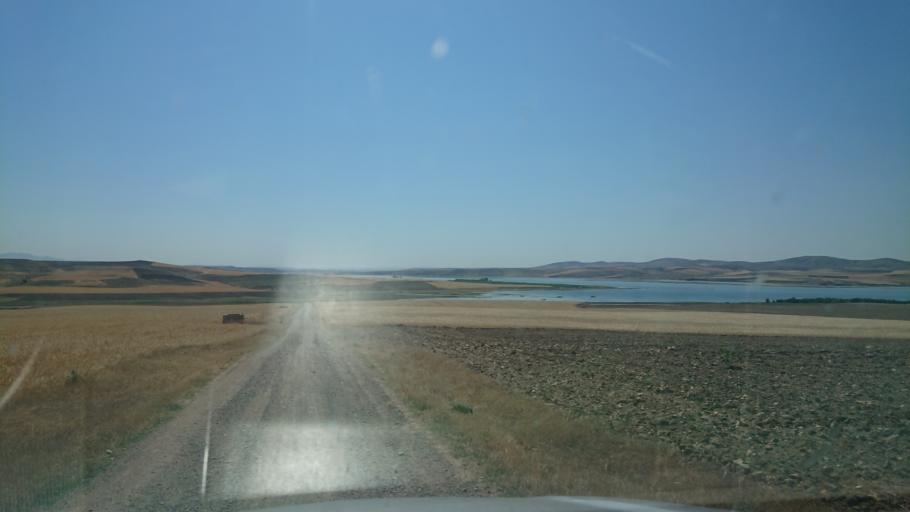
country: TR
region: Aksaray
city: Sariyahsi
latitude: 39.0558
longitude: 33.8921
